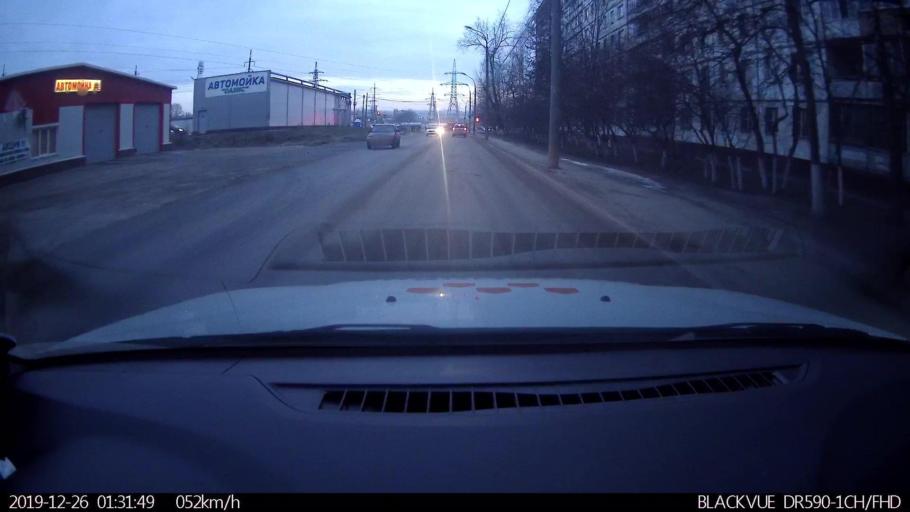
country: RU
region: Nizjnij Novgorod
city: Nizhniy Novgorod
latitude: 56.2650
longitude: 43.9024
